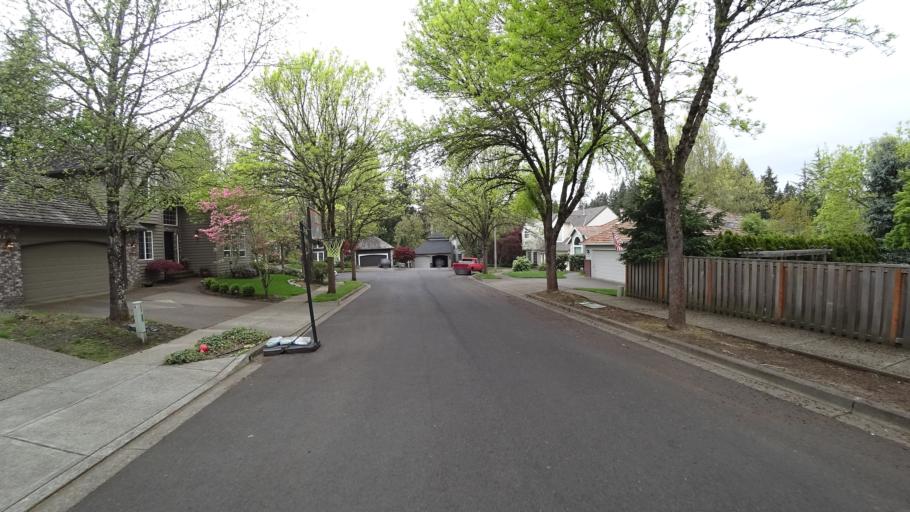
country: US
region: Oregon
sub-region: Washington County
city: Beaverton
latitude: 45.4610
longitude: -122.8300
